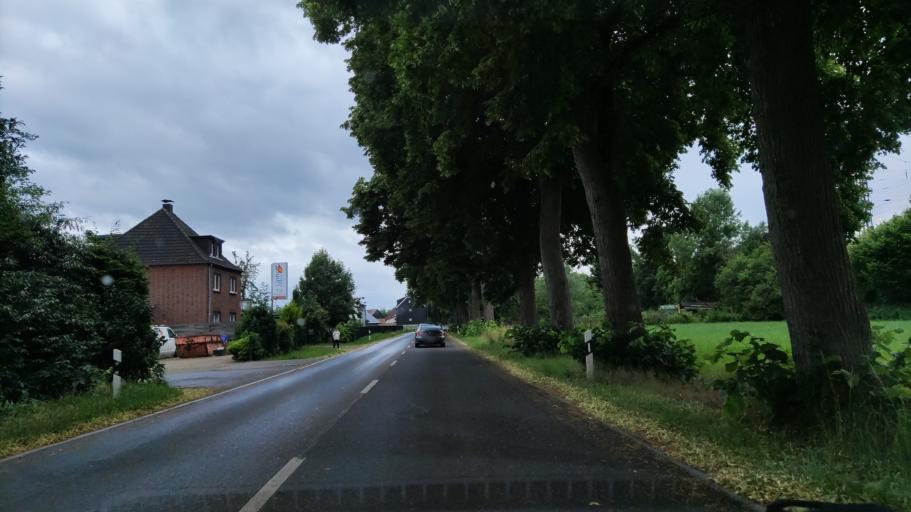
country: DE
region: North Rhine-Westphalia
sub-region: Regierungsbezirk Arnsberg
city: Hamm
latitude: 51.7144
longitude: 7.8389
